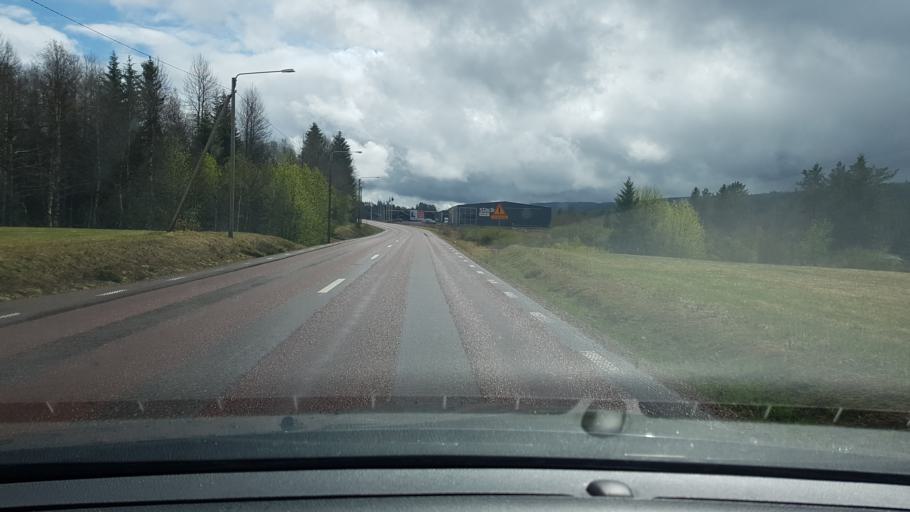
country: SE
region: Dalarna
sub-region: Malung-Saelens kommun
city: Malung
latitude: 61.1385
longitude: 13.2795
